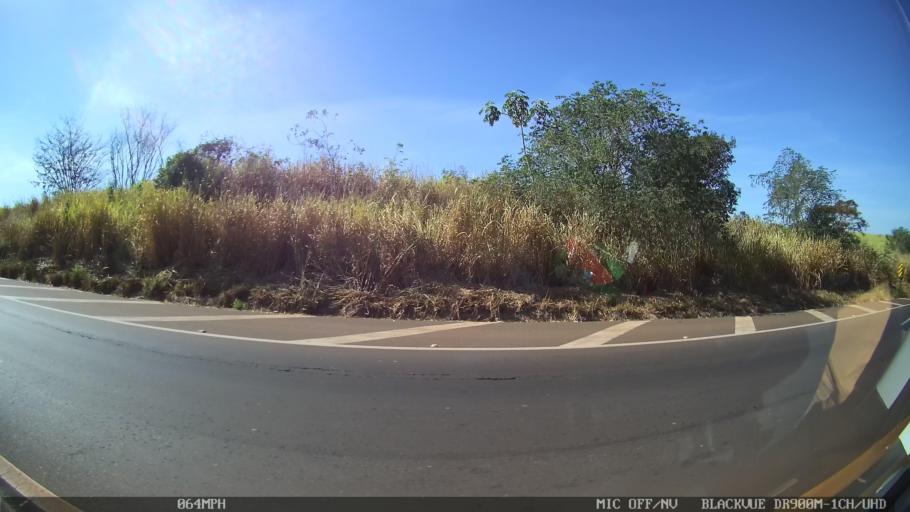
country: BR
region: Sao Paulo
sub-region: Olimpia
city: Olimpia
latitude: -20.6912
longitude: -48.8983
